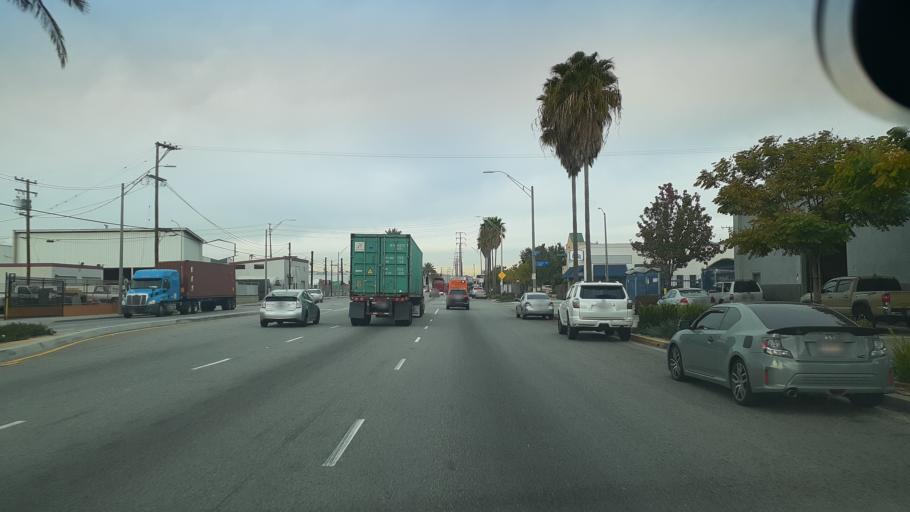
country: US
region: California
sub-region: Los Angeles County
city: Long Beach
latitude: 33.7828
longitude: -118.2130
